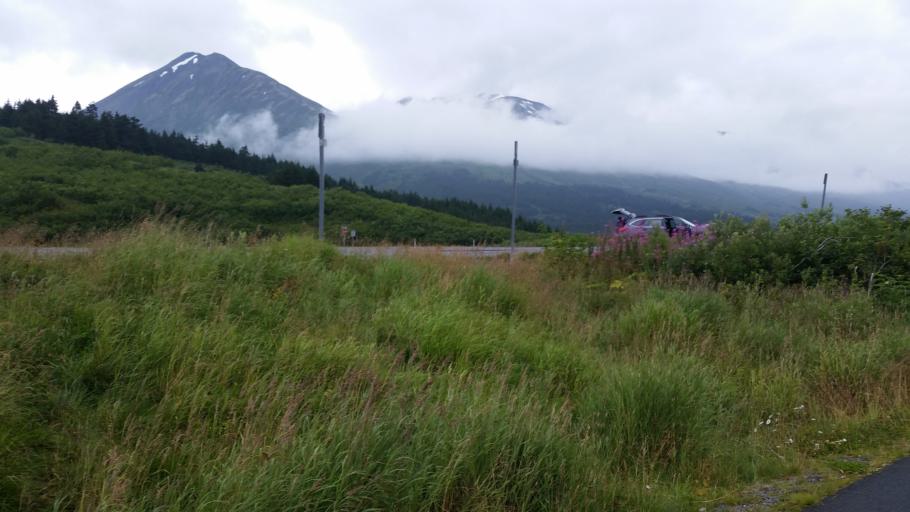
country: US
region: Alaska
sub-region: Anchorage Municipality
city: Girdwood
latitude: 60.7873
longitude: -149.2145
